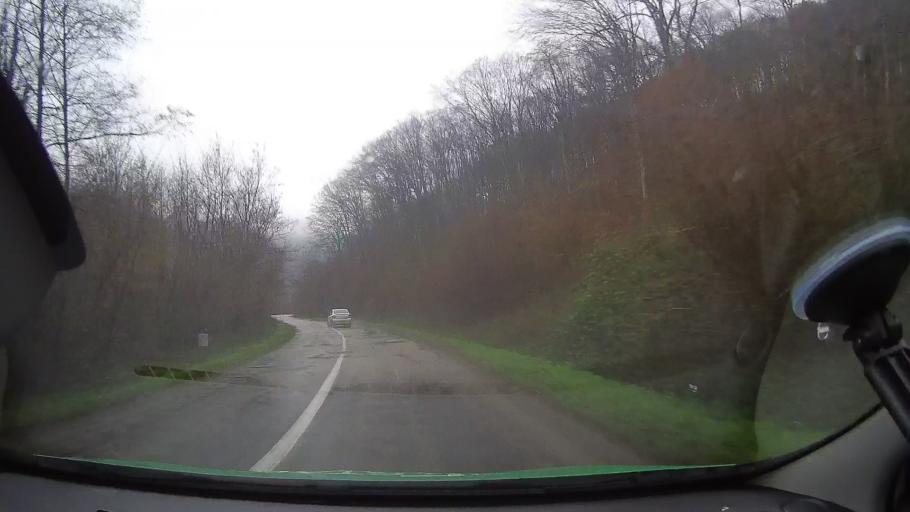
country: RO
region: Arad
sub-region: Comuna Dezna
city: Dezna
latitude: 46.4086
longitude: 22.2588
